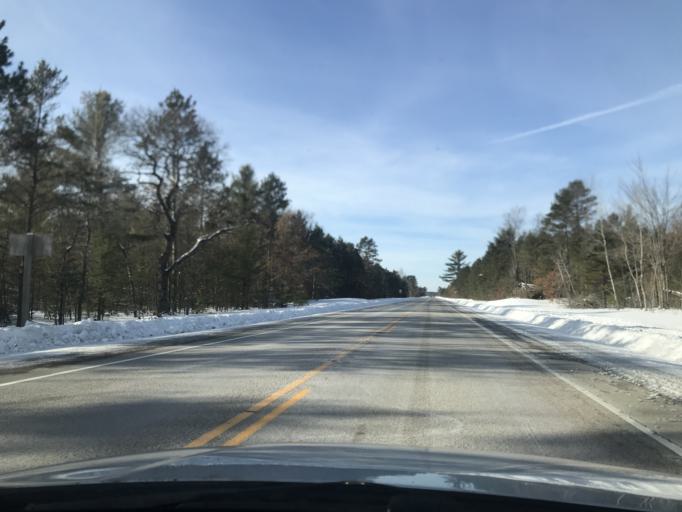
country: US
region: Wisconsin
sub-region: Oconto County
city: Gillett
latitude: 45.1161
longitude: -88.3801
